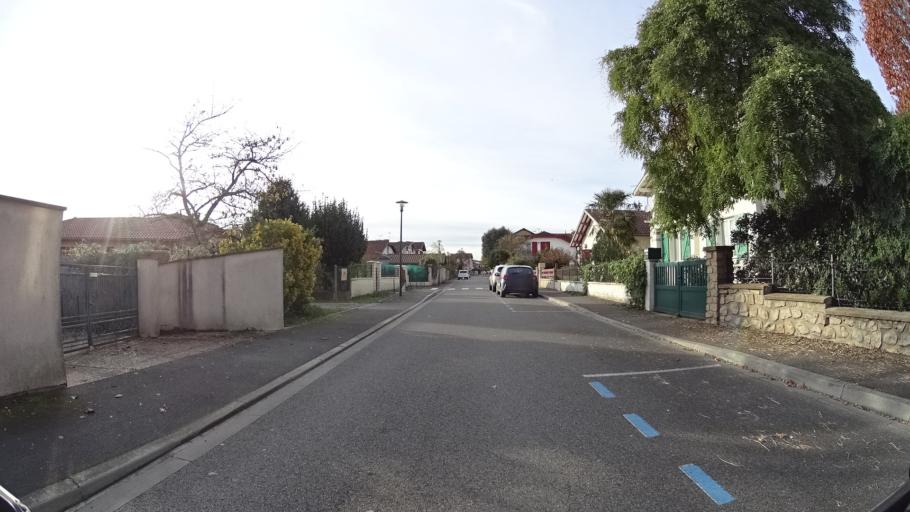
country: FR
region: Aquitaine
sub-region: Departement des Landes
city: Saint-Paul-les-Dax
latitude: 43.7223
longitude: -1.0476
